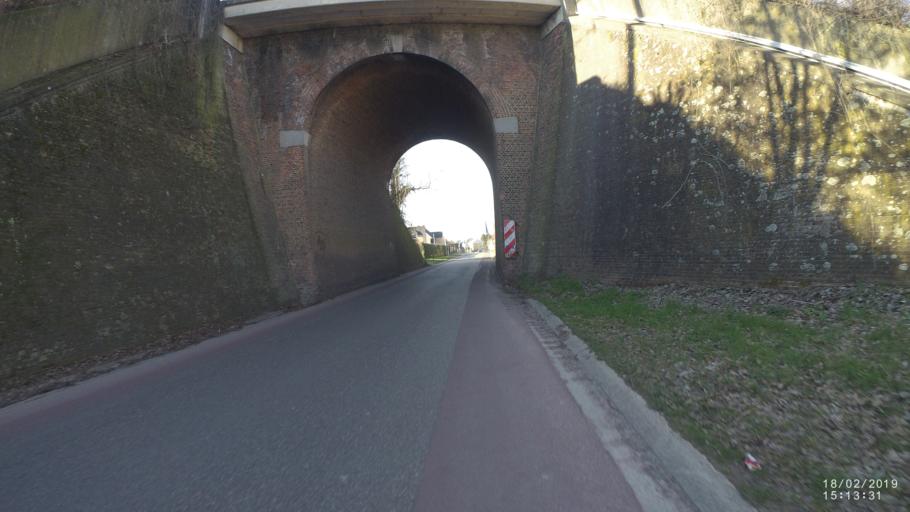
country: BE
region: Flanders
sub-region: Provincie Limburg
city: Hasselt
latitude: 50.9403
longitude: 5.3122
